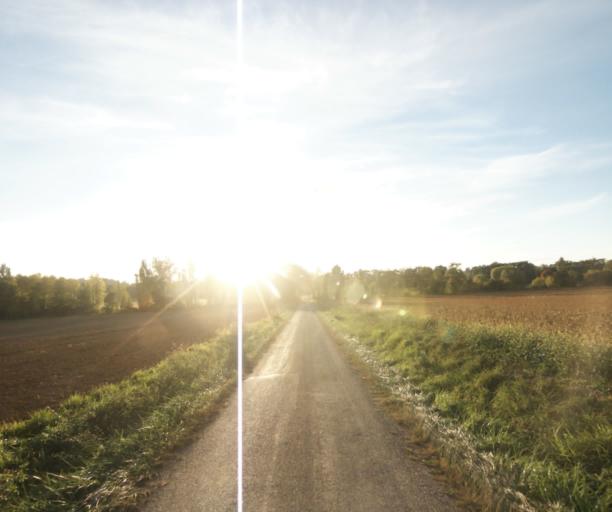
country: FR
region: Midi-Pyrenees
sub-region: Departement du Gers
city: Gondrin
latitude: 43.8615
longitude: 0.2824
